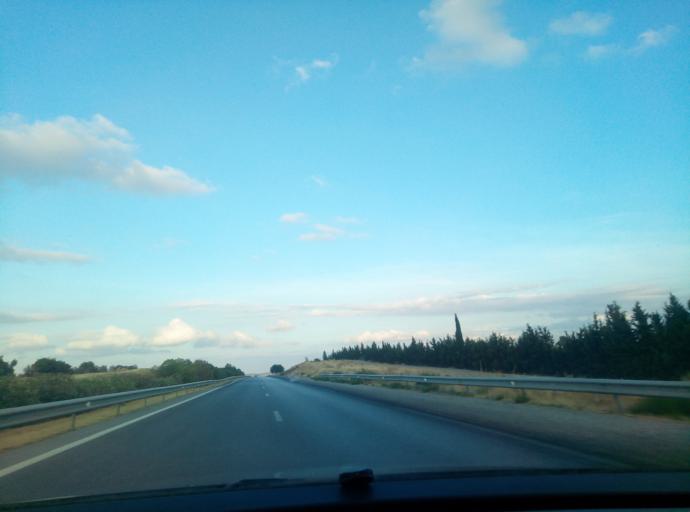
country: TN
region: Manouba
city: El Battan
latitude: 36.6596
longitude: 9.8176
